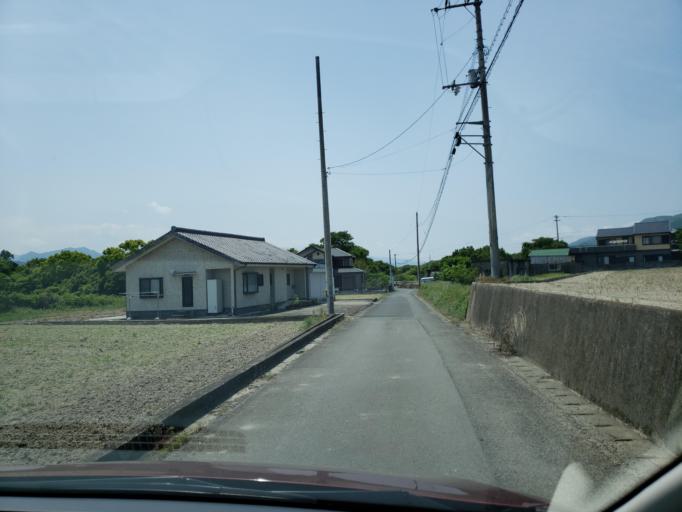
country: JP
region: Tokushima
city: Wakimachi
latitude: 34.0861
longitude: 134.2099
